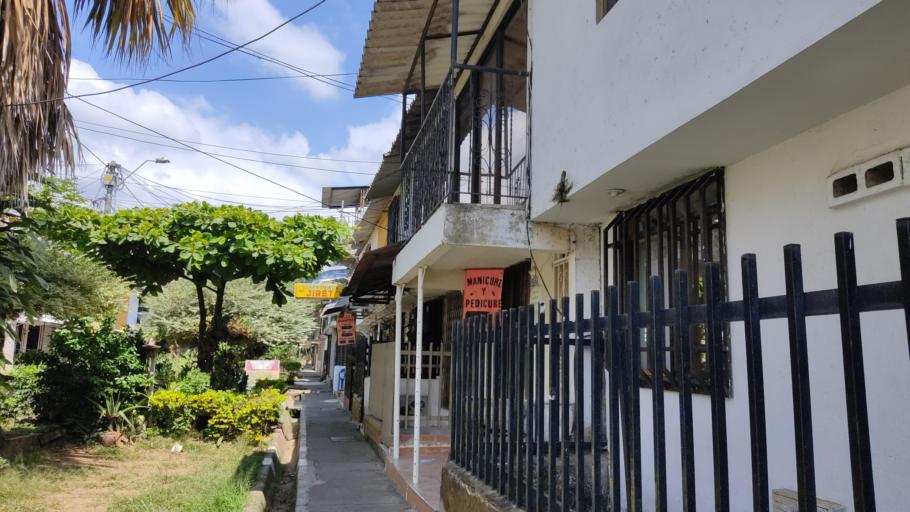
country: CO
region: Valle del Cauca
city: Jamundi
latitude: 3.2531
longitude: -76.5418
